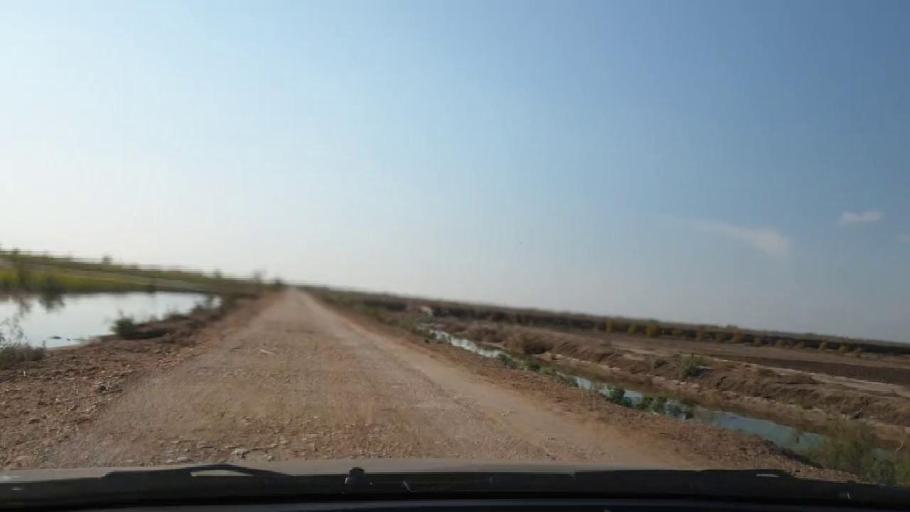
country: PK
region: Sindh
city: Khadro
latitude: 26.1563
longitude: 68.7960
